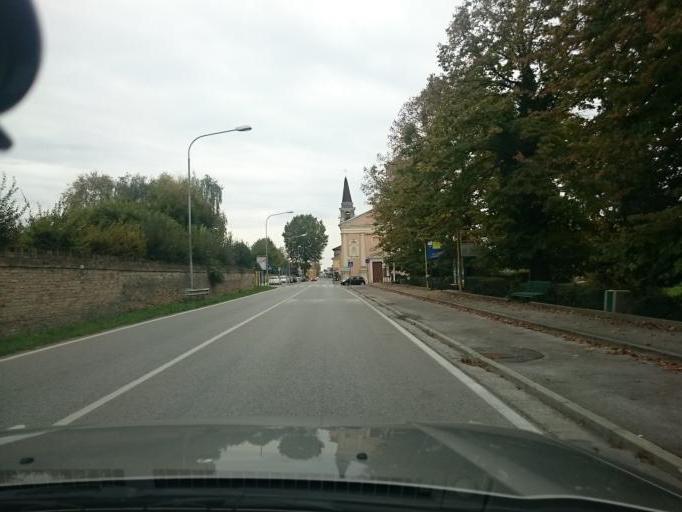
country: IT
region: Veneto
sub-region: Provincia di Padova
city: Arzergrande
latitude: 45.2758
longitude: 12.0287
